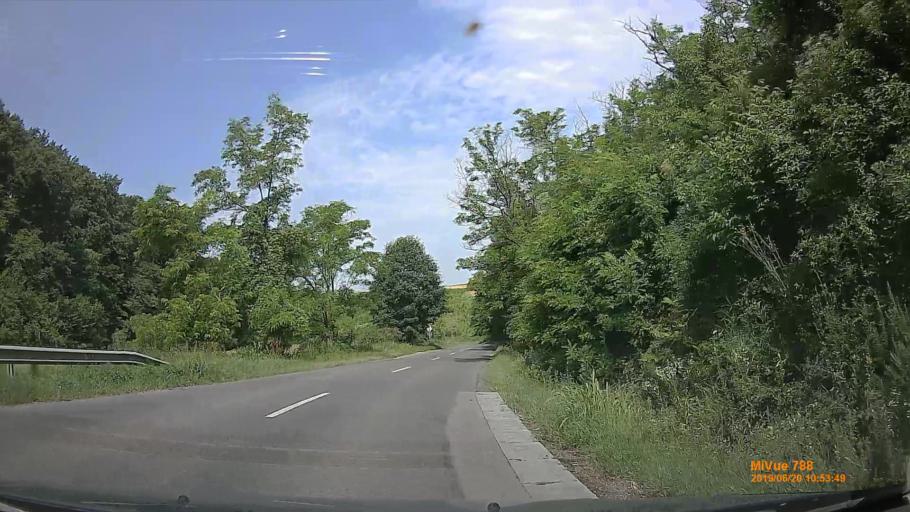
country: HU
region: Baranya
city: Mecseknadasd
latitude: 46.1554
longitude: 18.5701
